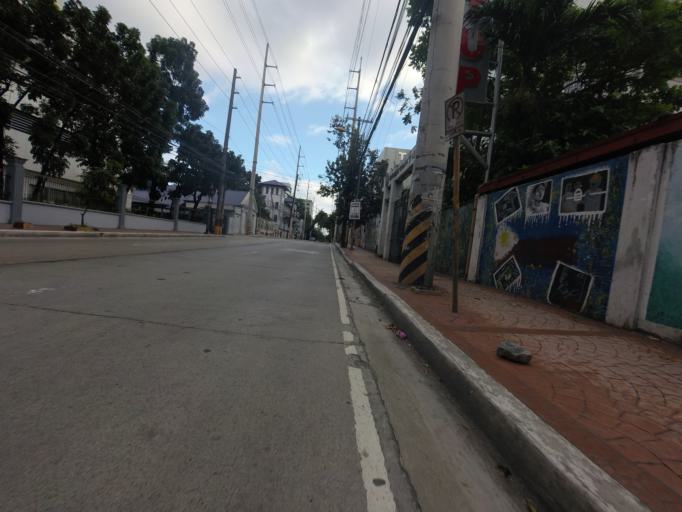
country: PH
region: Metro Manila
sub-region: City of Manila
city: Quiapo
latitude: 14.5868
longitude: 120.9854
